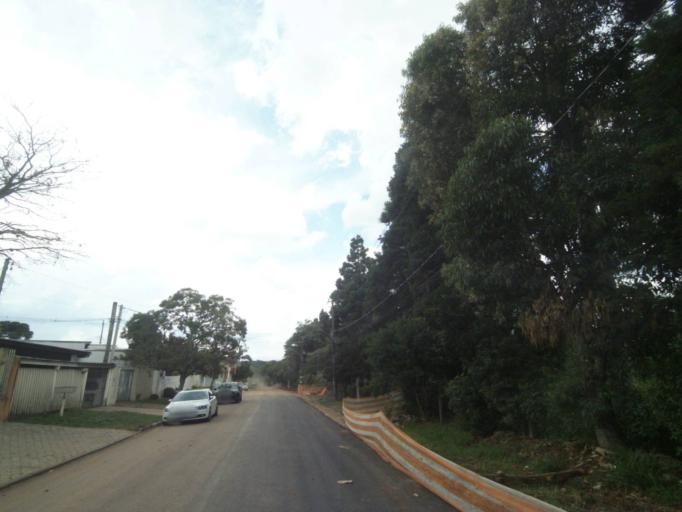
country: BR
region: Parana
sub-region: Curitiba
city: Curitiba
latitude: -25.4658
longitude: -49.3434
